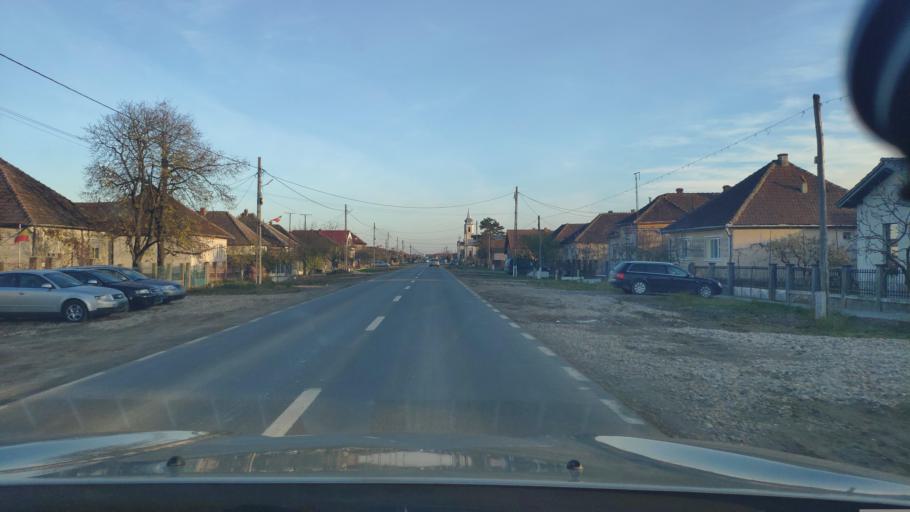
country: RO
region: Satu Mare
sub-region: Comuna Mediesu Aurit
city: Potau
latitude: 47.7779
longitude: 23.0914
